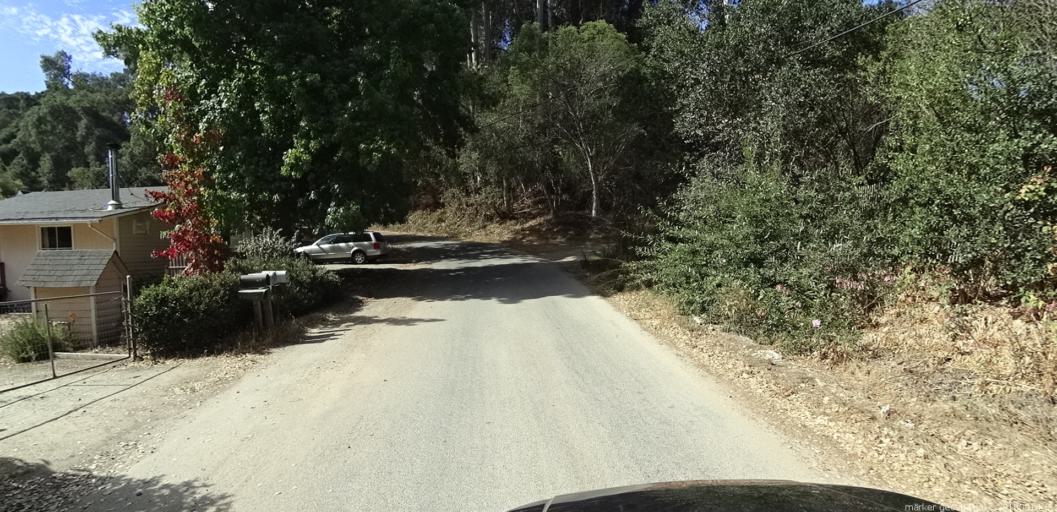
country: US
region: California
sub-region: San Benito County
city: Aromas
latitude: 36.8555
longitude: -121.6491
